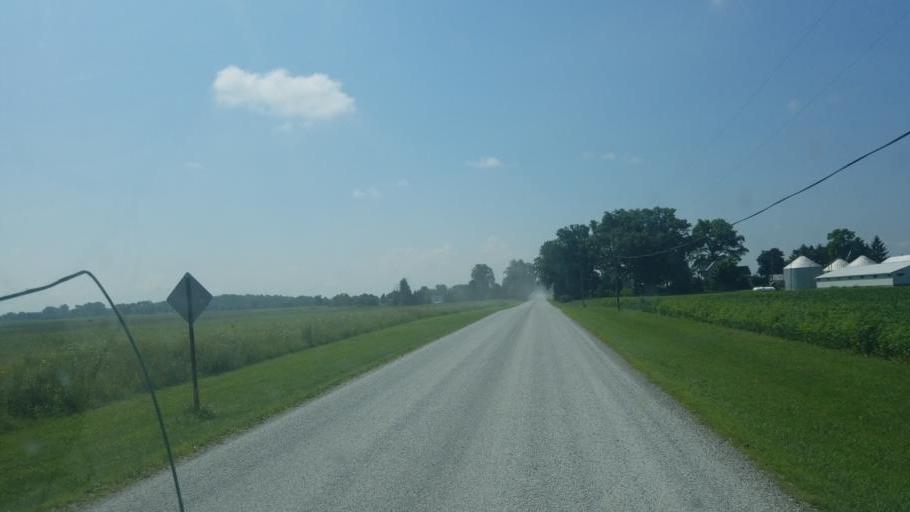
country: US
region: Ohio
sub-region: Hardin County
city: Ada
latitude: 40.6837
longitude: -83.7304
